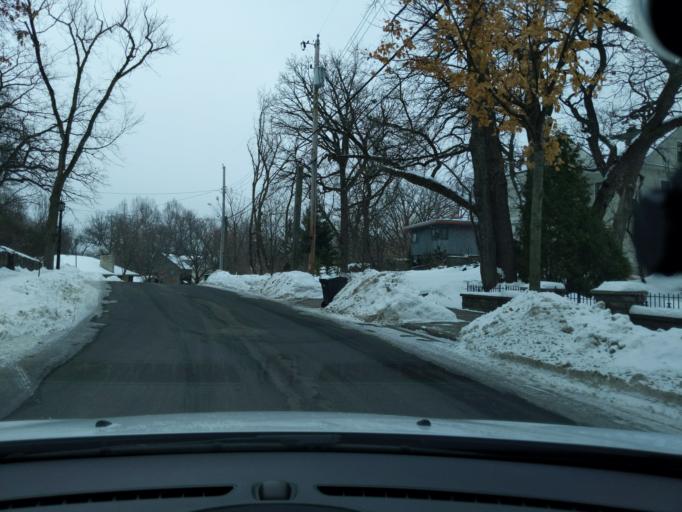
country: US
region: Minnesota
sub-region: Ramsey County
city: Lauderdale
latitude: 44.9672
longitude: -93.2137
